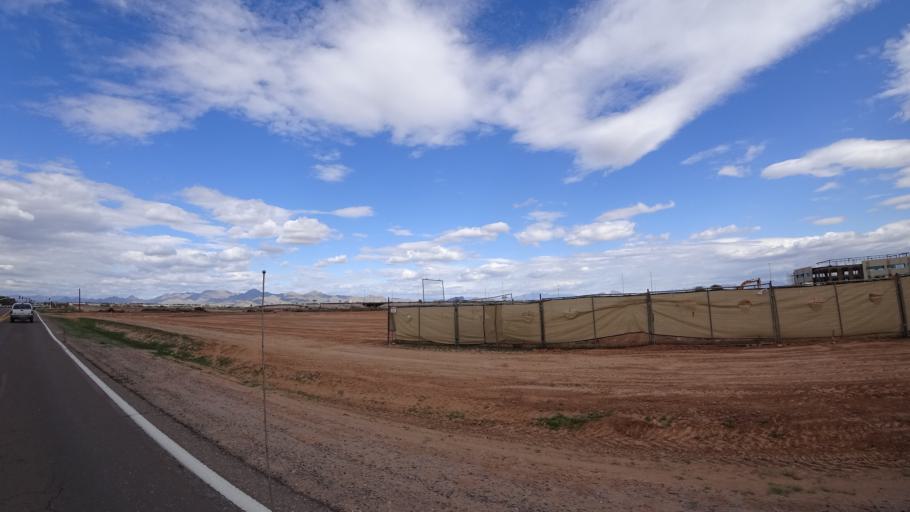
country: US
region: Arizona
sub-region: Maricopa County
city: Scottsdale
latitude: 33.5207
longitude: -111.8915
